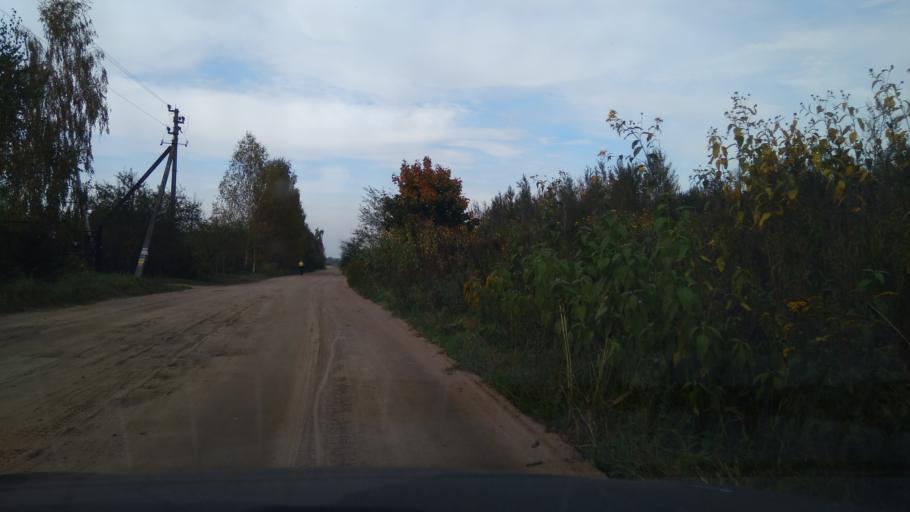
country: BY
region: Minsk
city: Rudzyensk
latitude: 53.6113
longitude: 27.8476
